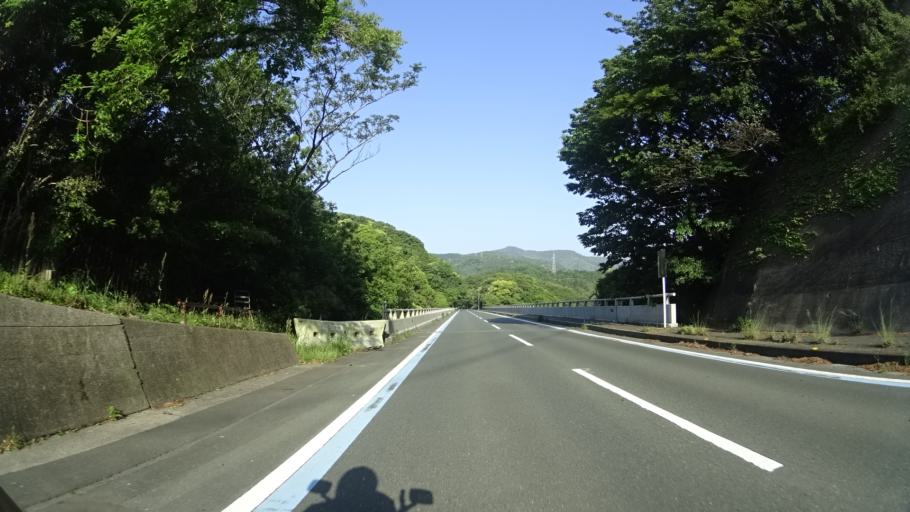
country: JP
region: Ehime
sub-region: Nishiuwa-gun
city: Ikata-cho
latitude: 33.3963
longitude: 132.1478
